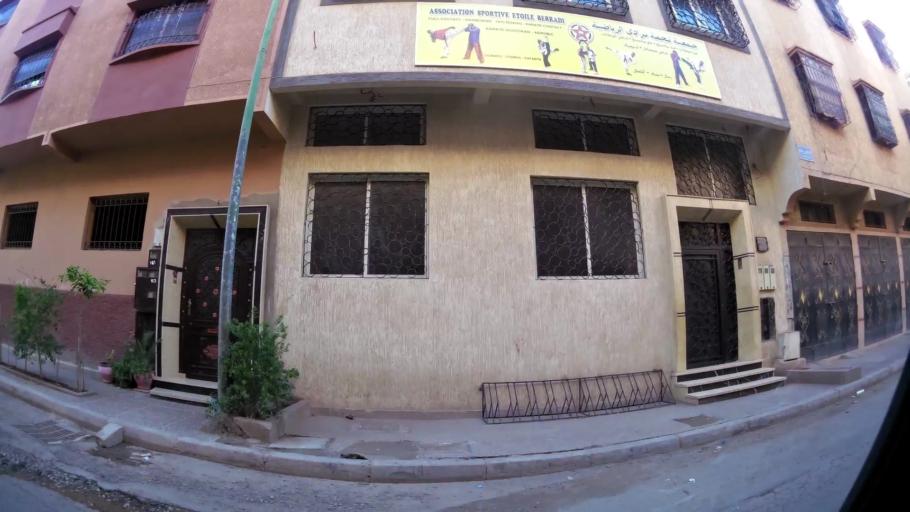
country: MA
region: Marrakech-Tensift-Al Haouz
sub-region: Marrakech
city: Marrakesh
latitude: 31.6207
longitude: -8.0690
